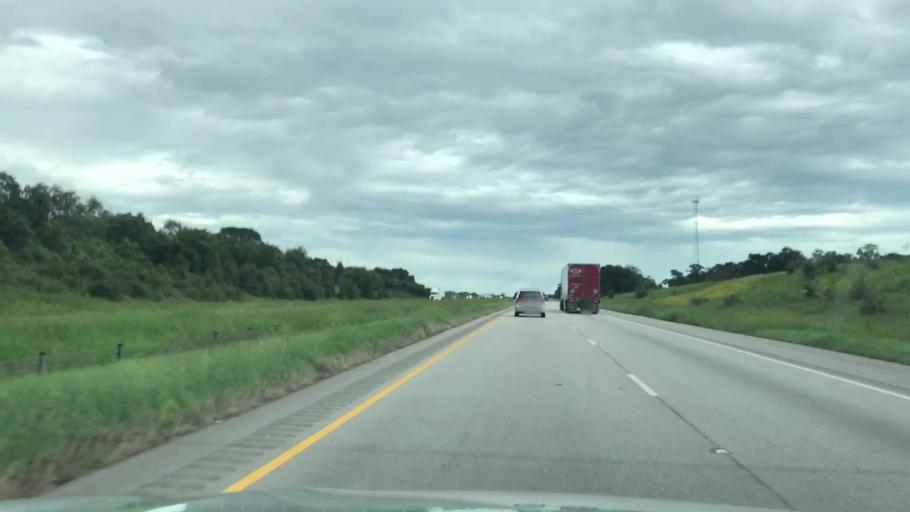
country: US
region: Texas
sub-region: Fayette County
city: Schulenburg
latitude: 29.6963
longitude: -96.8626
